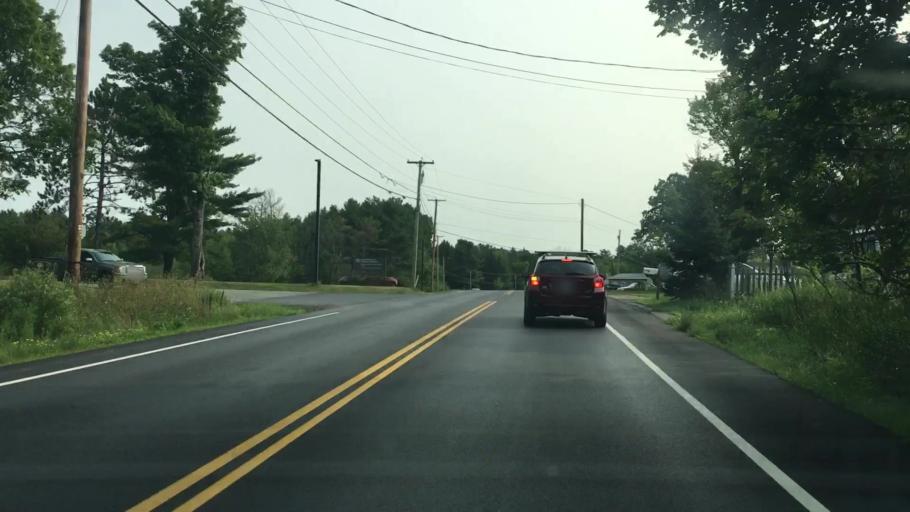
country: US
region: Maine
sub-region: Kennebec County
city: Chelsea
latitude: 44.2720
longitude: -69.6937
